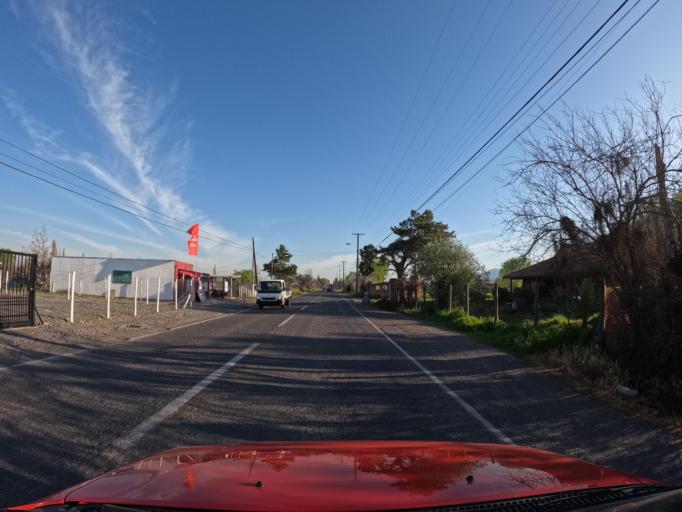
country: CL
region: Maule
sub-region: Provincia de Curico
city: Rauco
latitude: -34.8733
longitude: -71.2667
